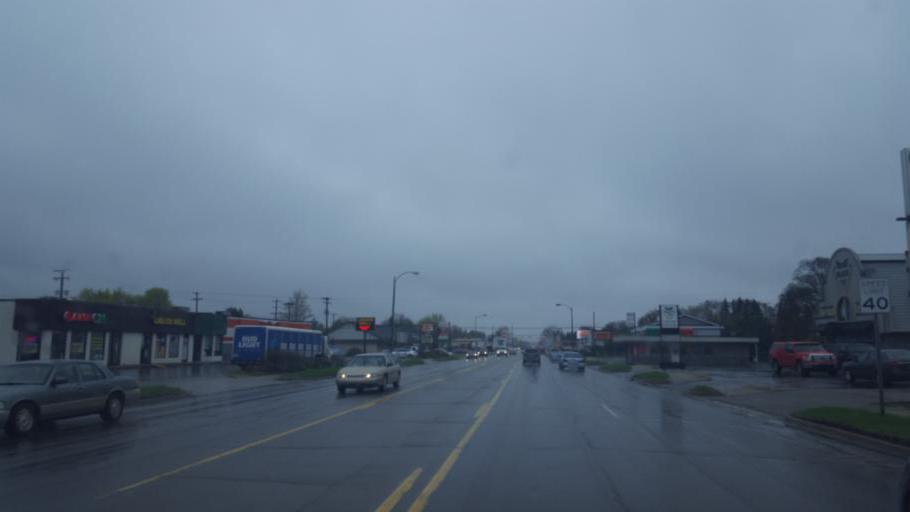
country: US
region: Michigan
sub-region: Isabella County
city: Mount Pleasant
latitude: 43.5941
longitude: -84.7675
